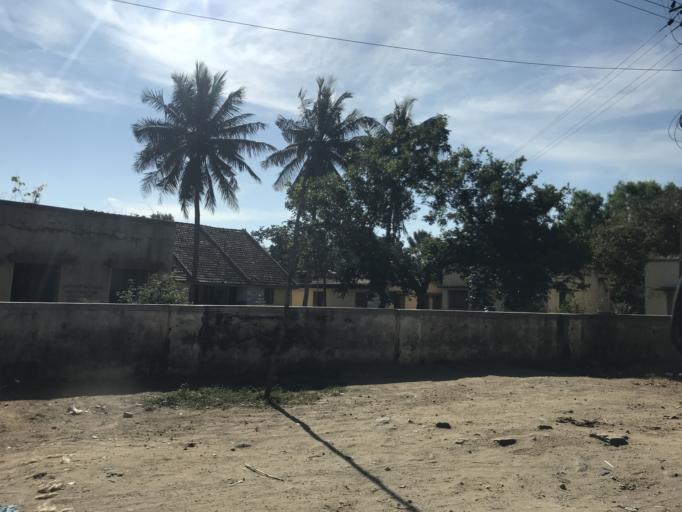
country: IN
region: Karnataka
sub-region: Mysore
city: Mysore
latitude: 12.2040
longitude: 76.5552
